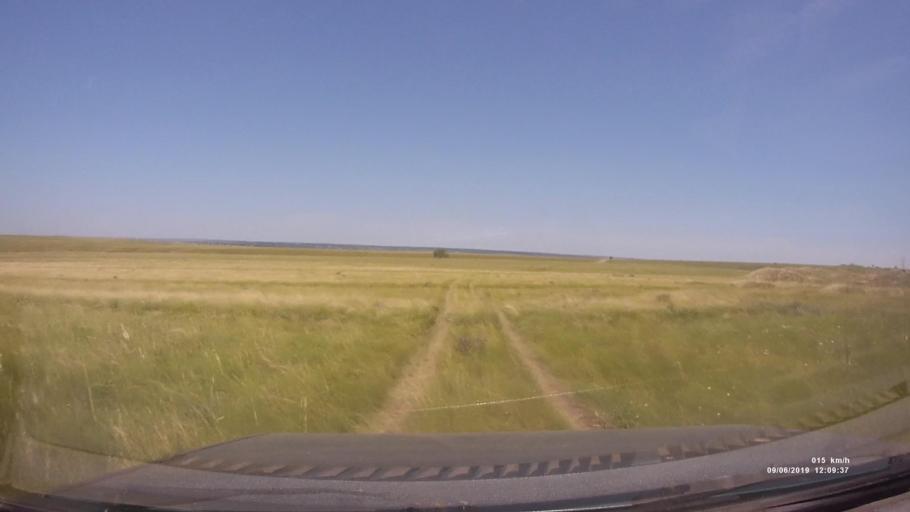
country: RU
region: Rostov
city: Staraya Stanitsa
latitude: 48.2484
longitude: 40.3380
